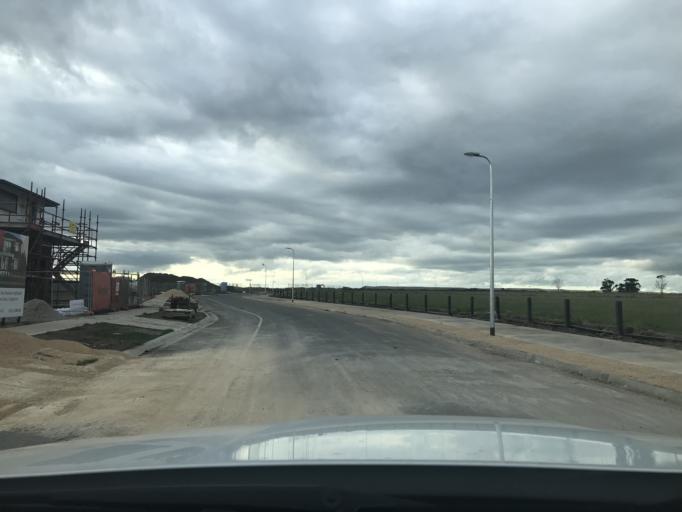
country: AU
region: Victoria
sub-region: Hume
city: Roxburgh Park
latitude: -37.5821
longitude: 144.9003
